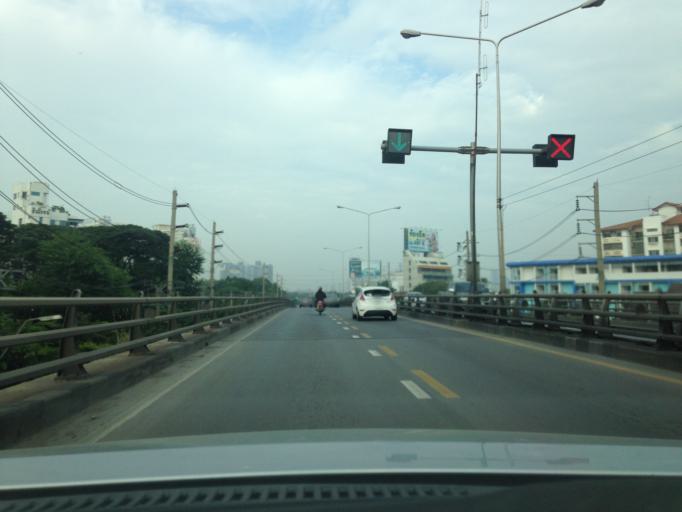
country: TH
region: Bangkok
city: Bang Sue
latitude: 13.8304
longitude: 100.5392
